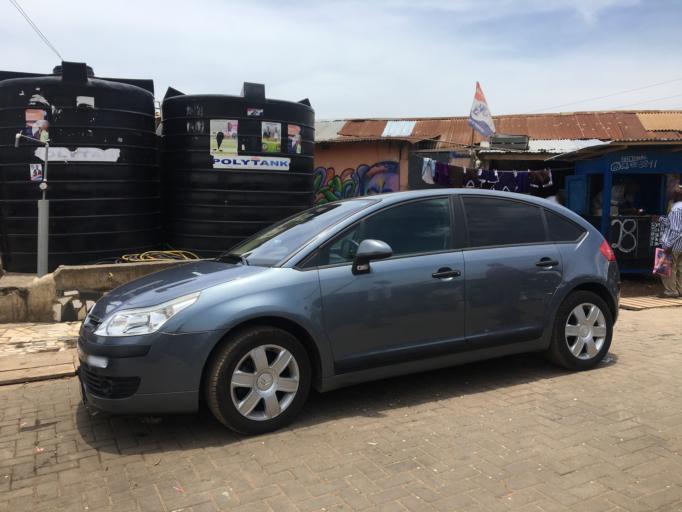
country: GH
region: Greater Accra
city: Accra
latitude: 5.5839
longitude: -0.1952
